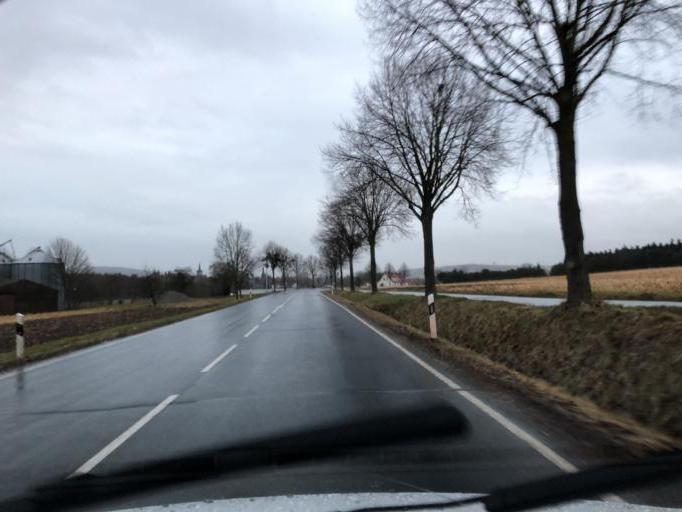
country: DE
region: Lower Saxony
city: Duderstadt
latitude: 51.5223
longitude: 10.2672
